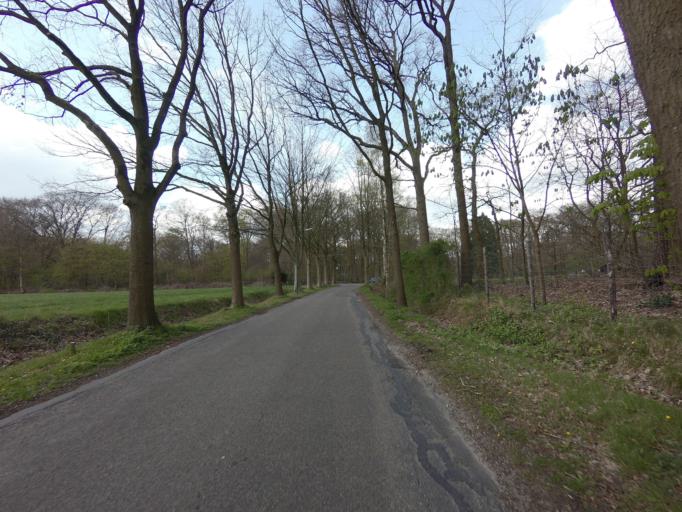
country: NL
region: Utrecht
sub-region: Gemeente Utrechtse Heuvelrug
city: Doorn
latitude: 52.0293
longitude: 5.3593
